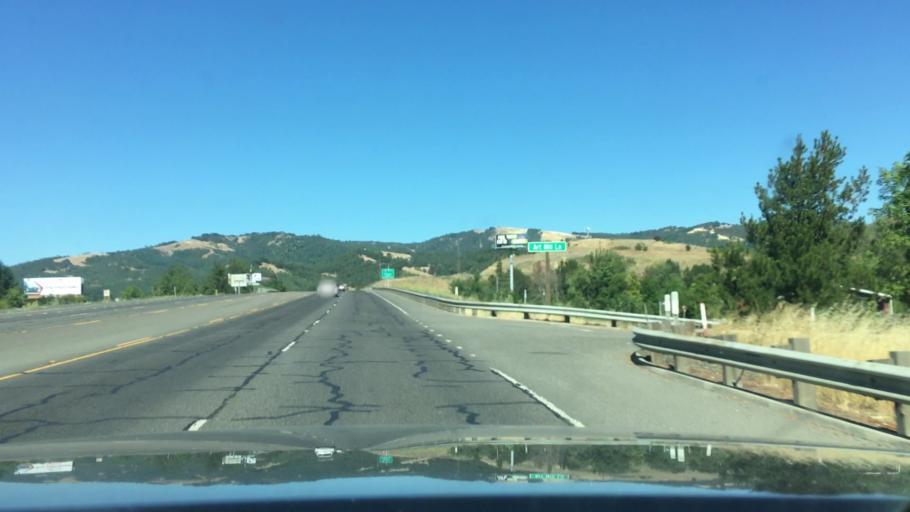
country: US
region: Oregon
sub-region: Douglas County
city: Green
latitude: 43.1466
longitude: -123.3792
